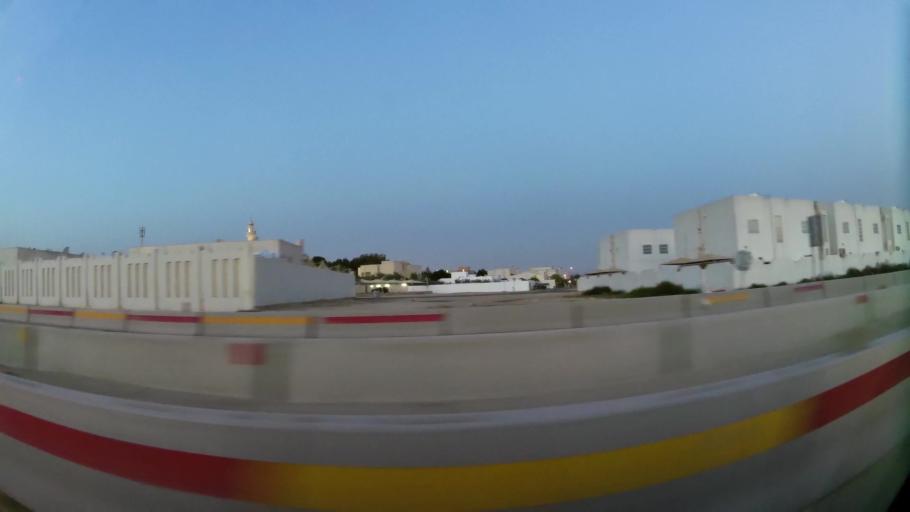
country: QA
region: Baladiyat ar Rayyan
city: Ar Rayyan
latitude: 25.3115
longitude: 51.4529
